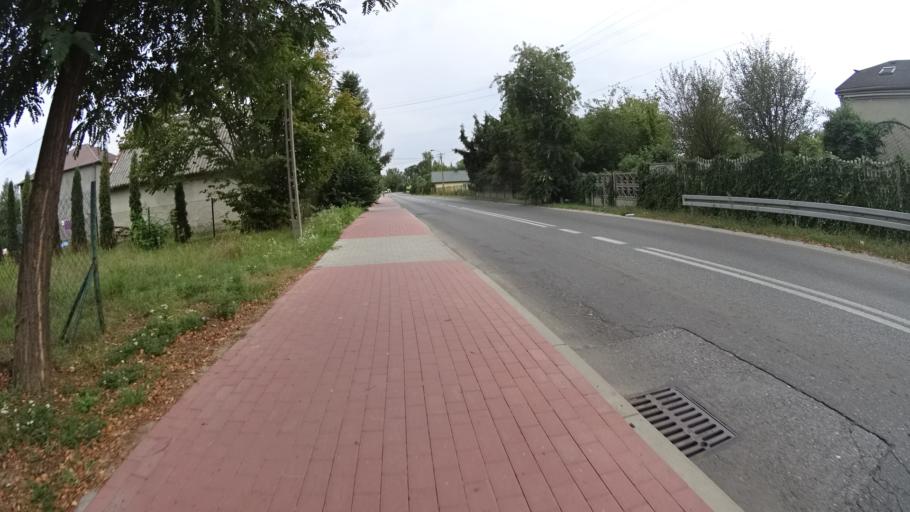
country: PL
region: Masovian Voivodeship
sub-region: Powiat pruszkowski
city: Granica
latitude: 52.1190
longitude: 20.7956
